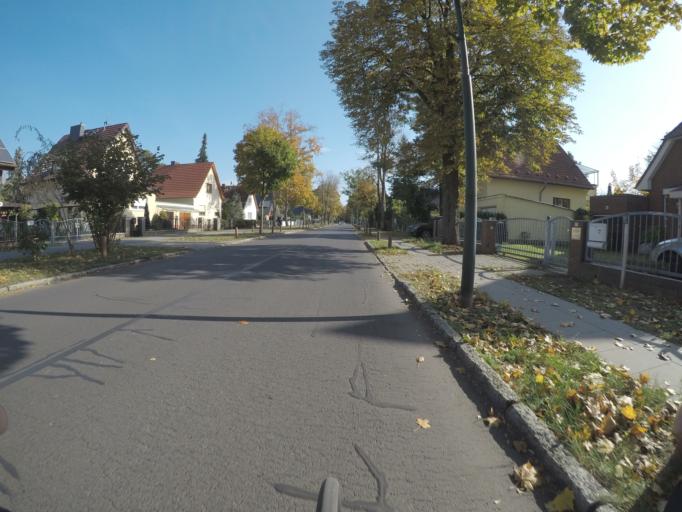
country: DE
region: Brandenburg
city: Hohen Neuendorf
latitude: 52.6783
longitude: 13.2545
